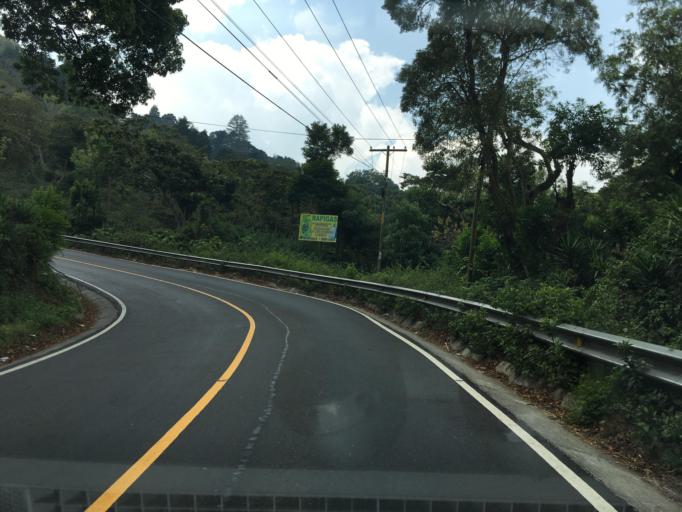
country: GT
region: Guatemala
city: Villa Canales
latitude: 14.4162
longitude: -90.5310
